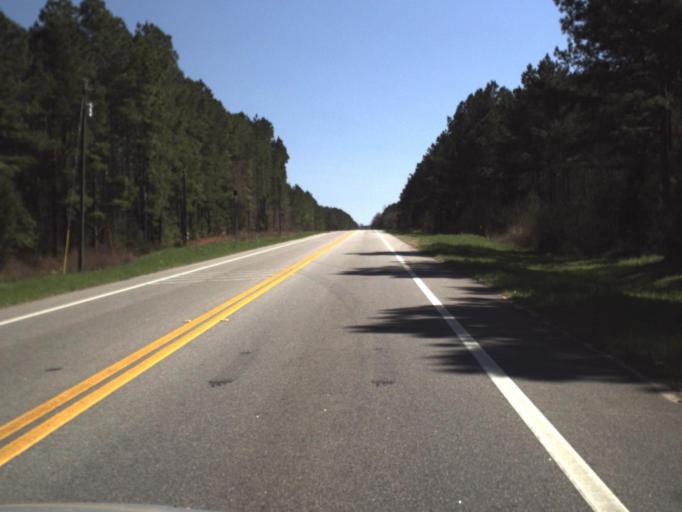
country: US
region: Florida
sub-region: Jackson County
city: Marianna
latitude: 30.8395
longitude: -85.3445
